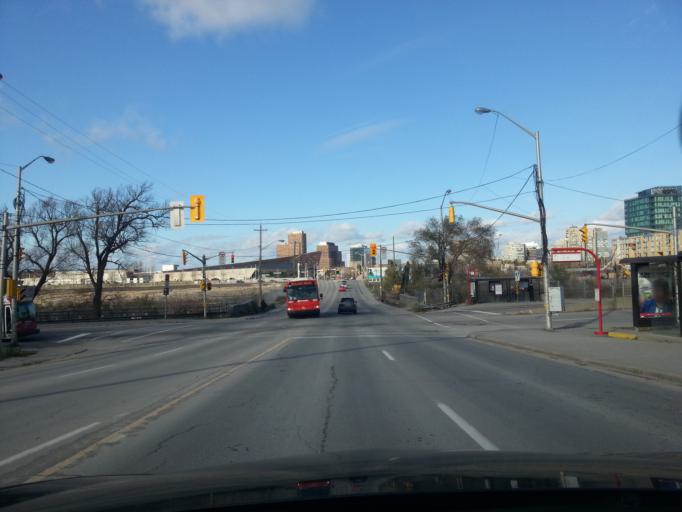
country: CA
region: Ontario
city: Ottawa
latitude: 45.4136
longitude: -75.7131
